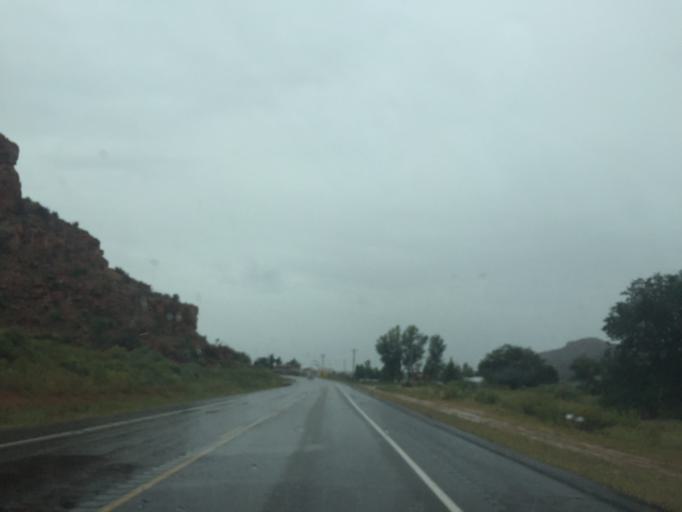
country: US
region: Utah
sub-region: Kane County
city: Kanab
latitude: 37.0618
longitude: -112.5370
